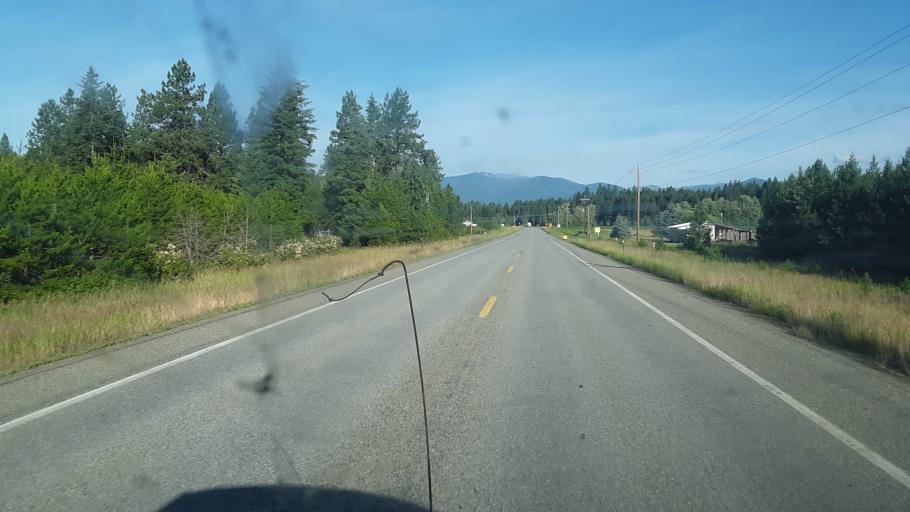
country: US
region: Idaho
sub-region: Boundary County
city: Bonners Ferry
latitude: 48.7300
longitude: -116.2347
